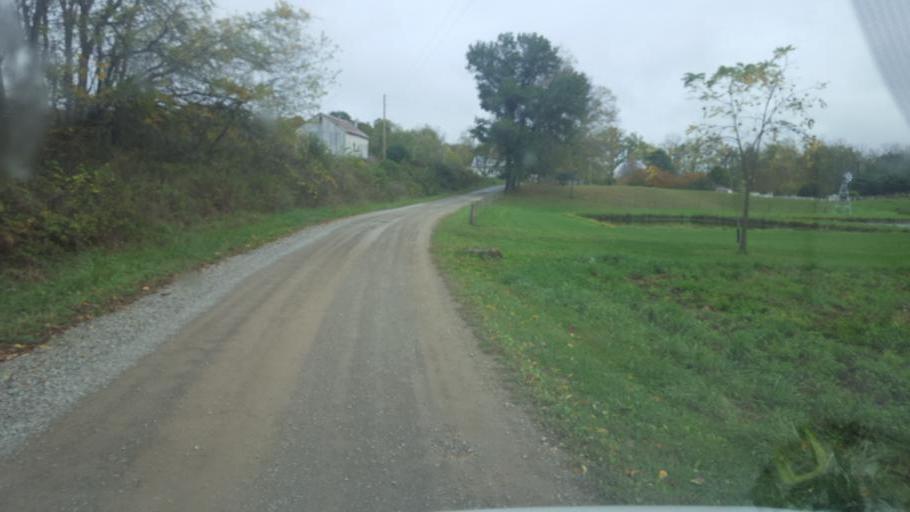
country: US
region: Ohio
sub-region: Wayne County
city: Shreve
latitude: 40.5969
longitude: -82.0371
